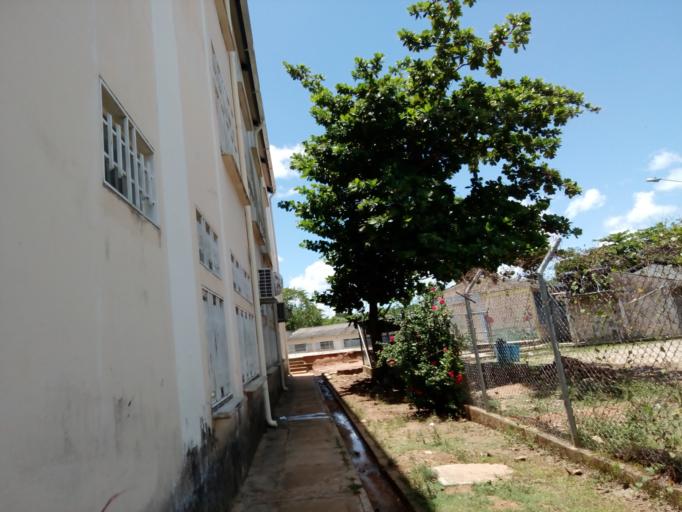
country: CO
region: Boyaca
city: Puerto Boyaca
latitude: 6.0669
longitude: -74.2678
